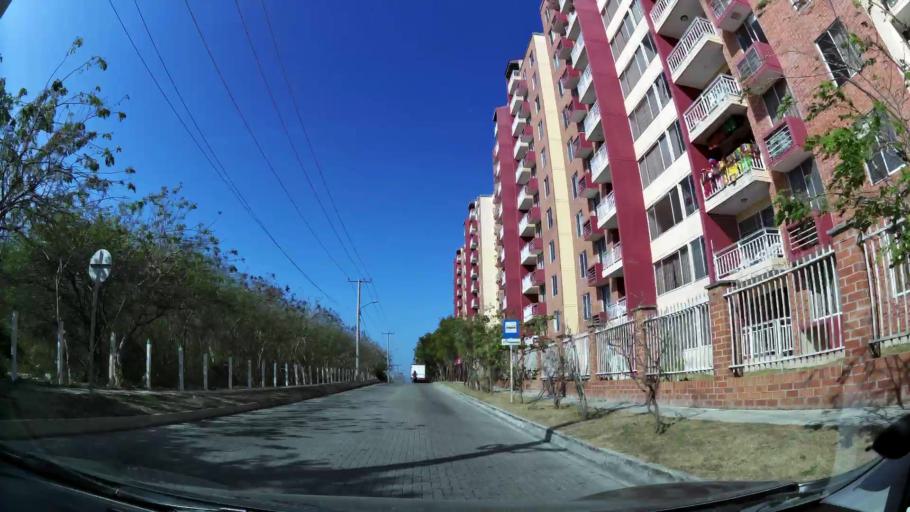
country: CO
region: Atlantico
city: Barranquilla
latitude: 11.0007
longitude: -74.8321
